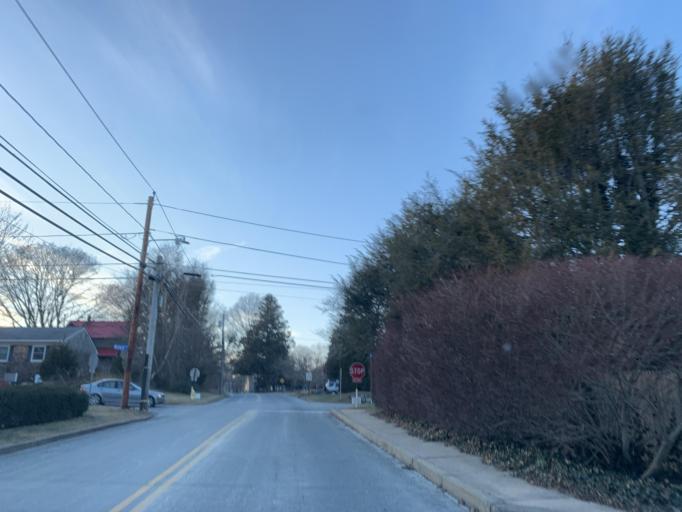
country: US
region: Rhode Island
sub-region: Washington County
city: Wakefield-Peacedale
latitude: 41.4457
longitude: -71.5067
